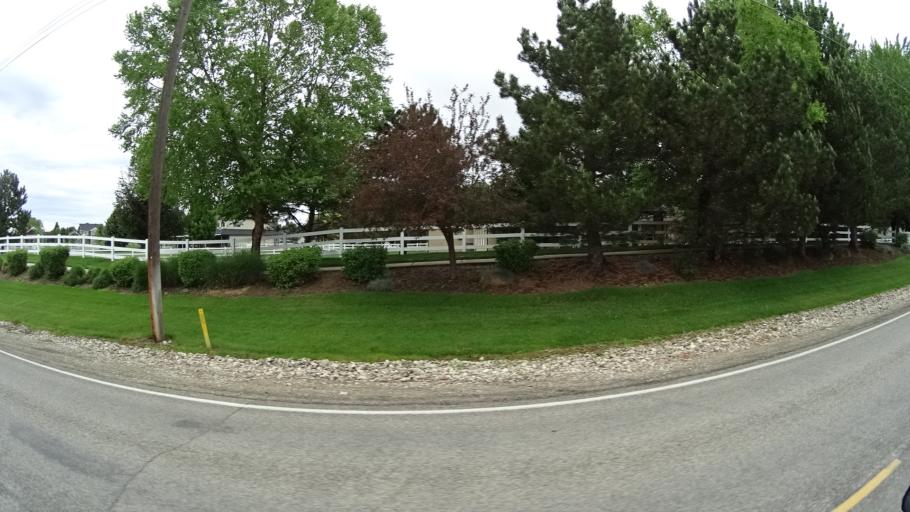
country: US
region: Idaho
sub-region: Ada County
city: Eagle
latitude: 43.7062
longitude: -116.3961
